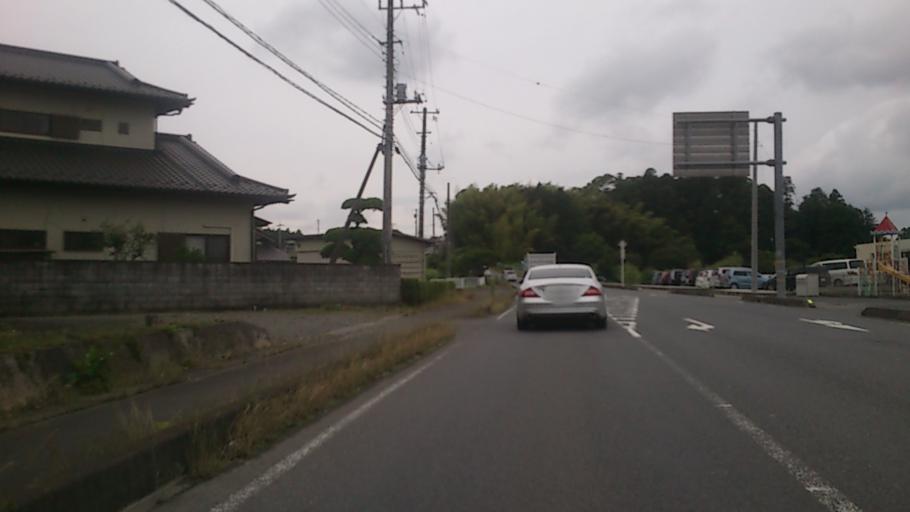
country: JP
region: Ibaraki
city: Okunoya
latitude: 36.2908
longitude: 140.3825
